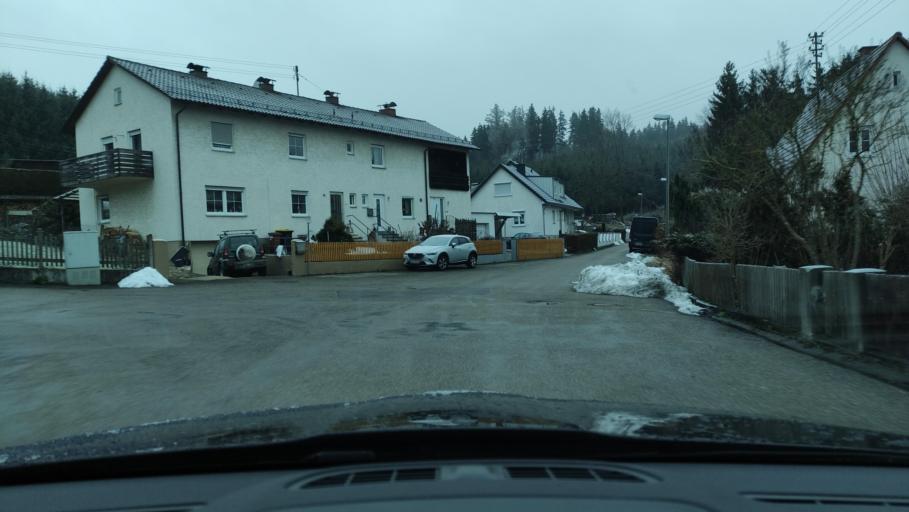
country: DE
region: Bavaria
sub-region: Swabia
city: Krumbach
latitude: 48.2530
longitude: 10.3512
